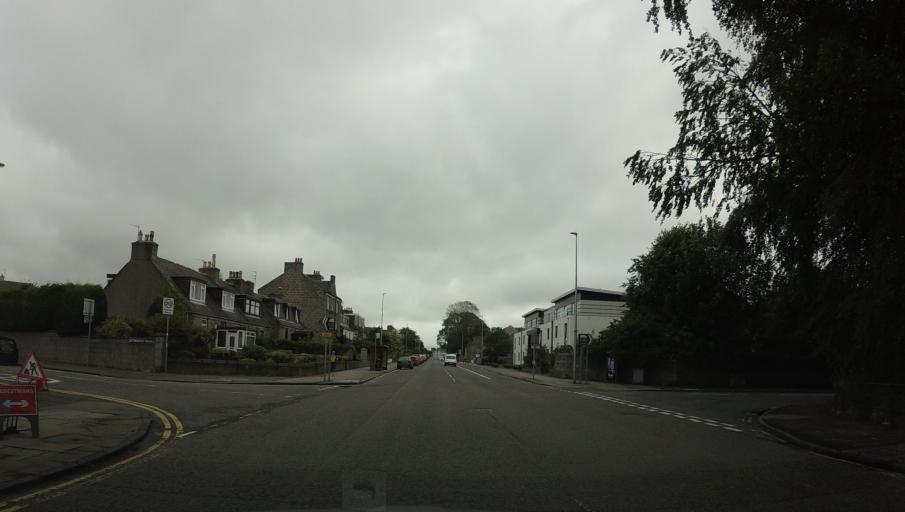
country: GB
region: Scotland
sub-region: Aberdeen City
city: Aberdeen
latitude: 57.1261
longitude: -2.1199
